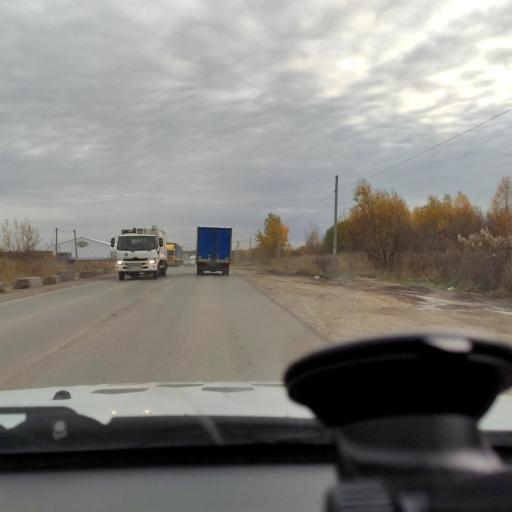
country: RU
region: Perm
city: Froly
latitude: 57.9565
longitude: 56.2785
